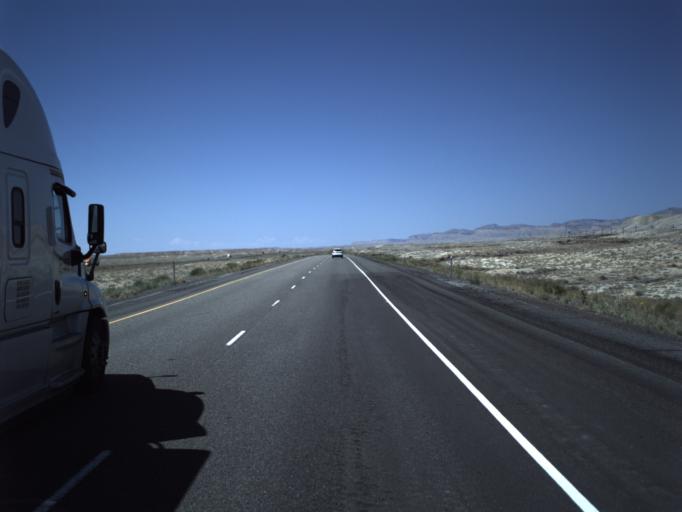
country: US
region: Utah
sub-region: Grand County
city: Moab
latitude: 38.9348
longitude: -109.4513
